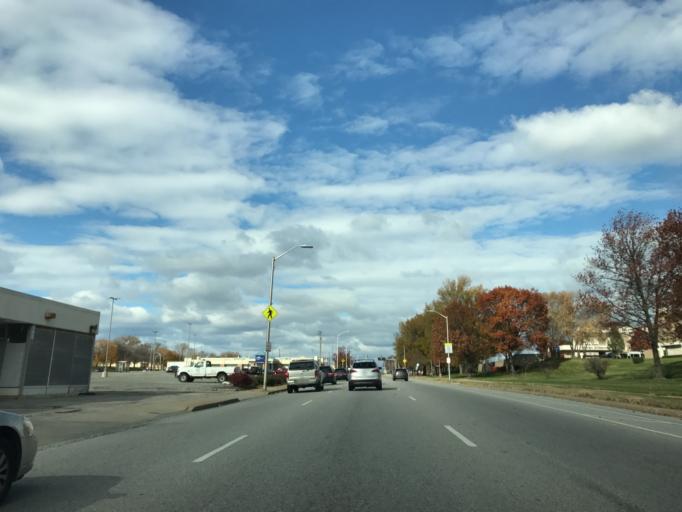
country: US
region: Maryland
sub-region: Anne Arundel County
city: Brooklyn Park
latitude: 39.2501
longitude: -76.6139
